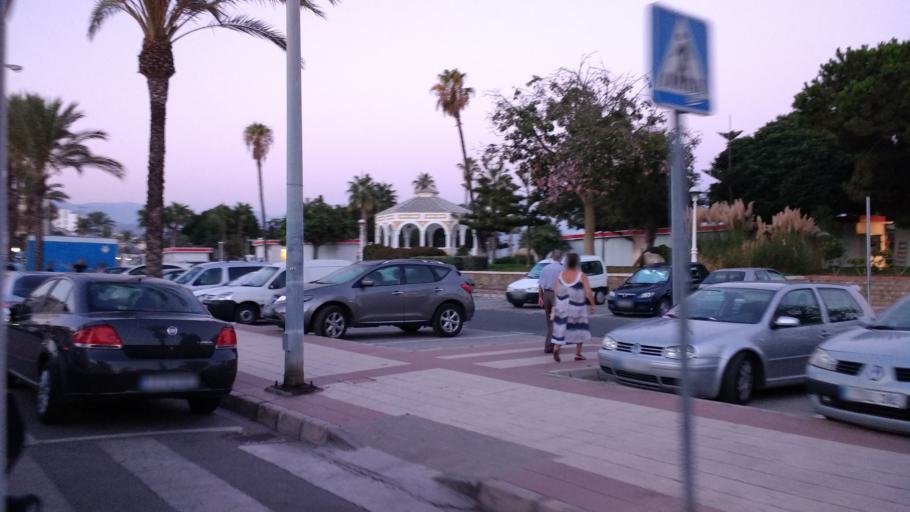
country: ES
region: Andalusia
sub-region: Provincia de Malaga
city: Velez-Malaga
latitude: 36.7372
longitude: -4.0949
